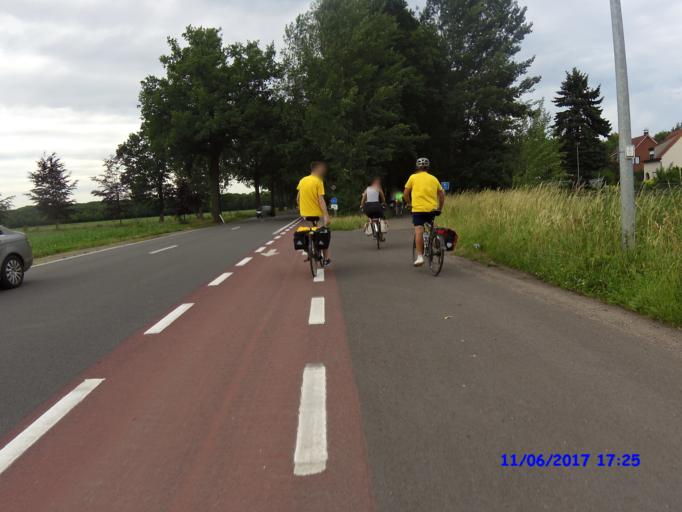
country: BE
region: Flanders
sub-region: Provincie Antwerpen
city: Turnhout
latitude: 51.3491
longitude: 4.9413
